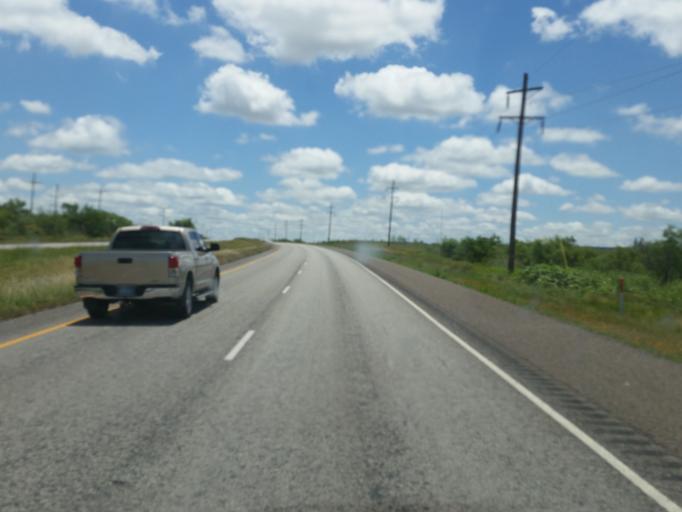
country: US
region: Texas
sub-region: Garza County
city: Post
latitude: 33.0027
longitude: -101.1627
